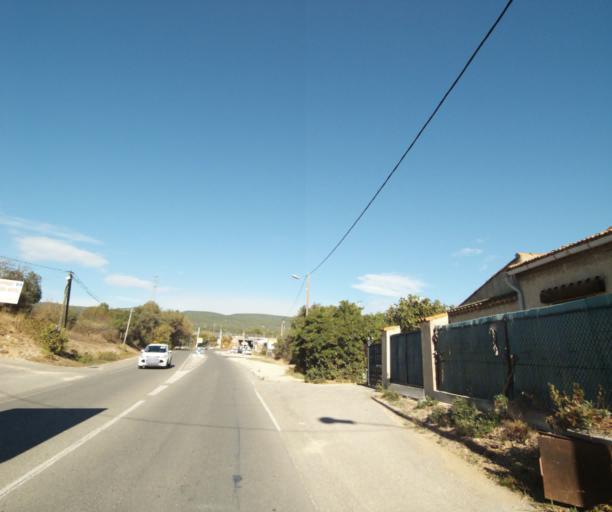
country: FR
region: Provence-Alpes-Cote d'Azur
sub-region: Departement des Bouches-du-Rhone
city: Ceyreste
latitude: 43.2071
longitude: 5.6276
